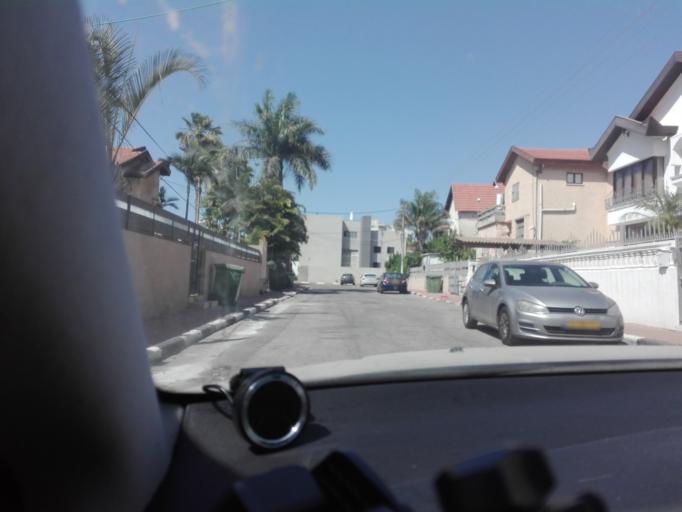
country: IL
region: Central District
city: Bene 'Ayish
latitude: 31.7268
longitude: 34.7429
